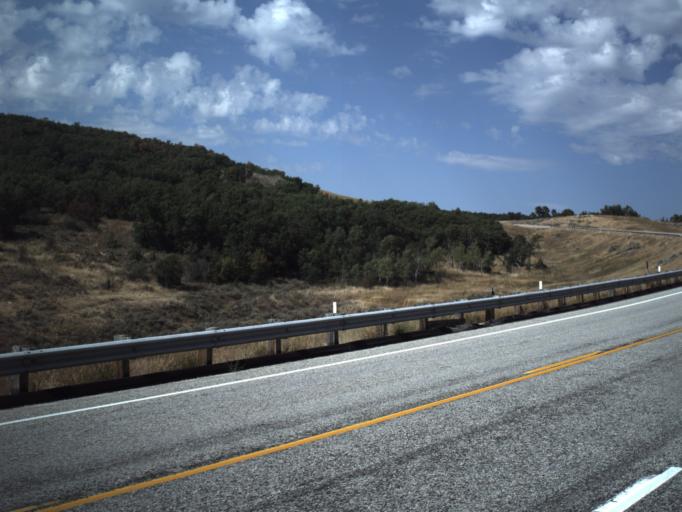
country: US
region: Utah
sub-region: Morgan County
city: Mountain Green
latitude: 41.1814
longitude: -111.8077
